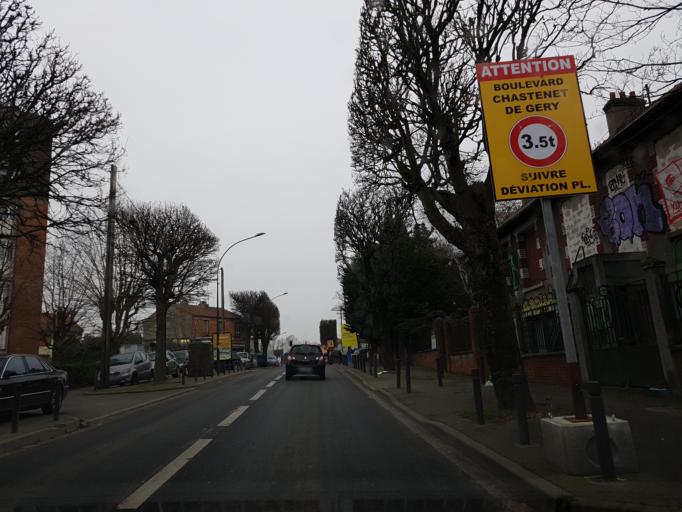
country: FR
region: Ile-de-France
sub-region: Departement du Val-de-Marne
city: Villejuif
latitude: 48.7955
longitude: 2.3530
